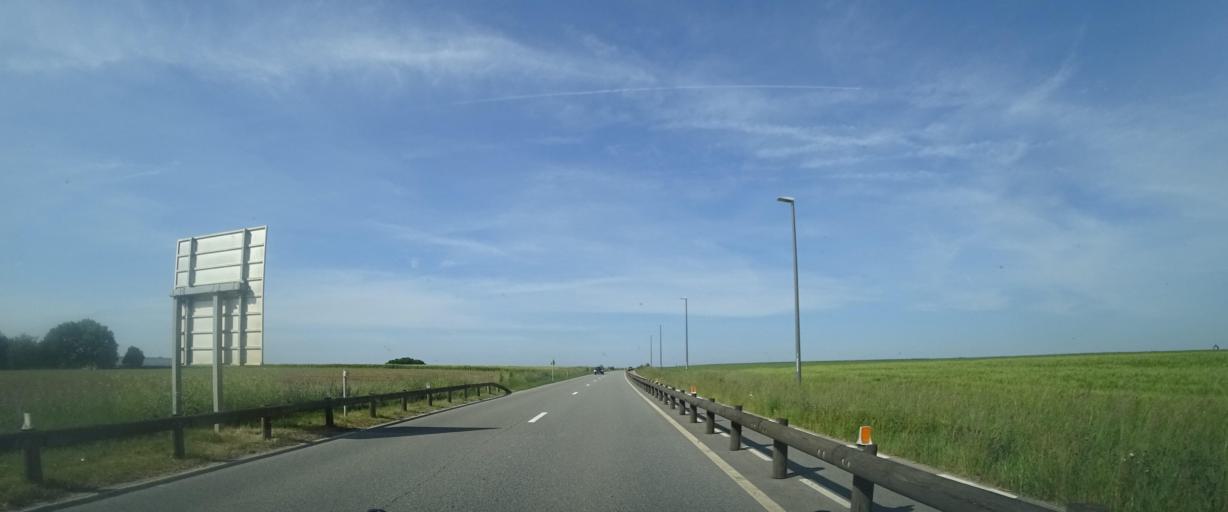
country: BE
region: Wallonia
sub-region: Province du Brabant Wallon
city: Chaumont-Gistoux
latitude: 50.6453
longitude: 4.7300
